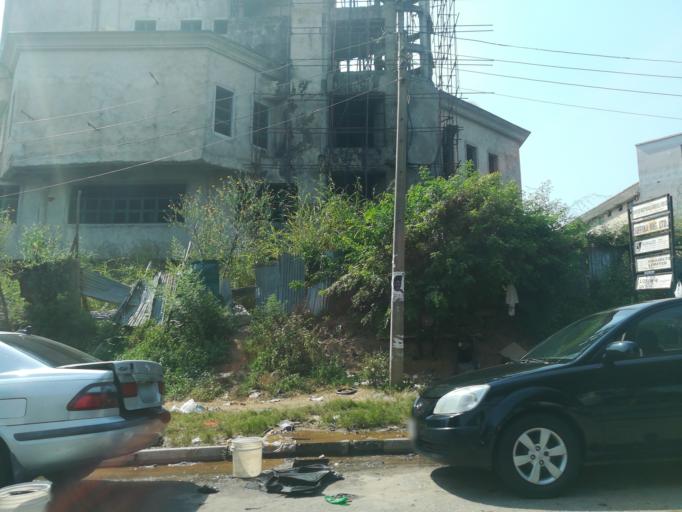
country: NG
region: Abuja Federal Capital Territory
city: Abuja
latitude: 9.0740
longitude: 7.4354
